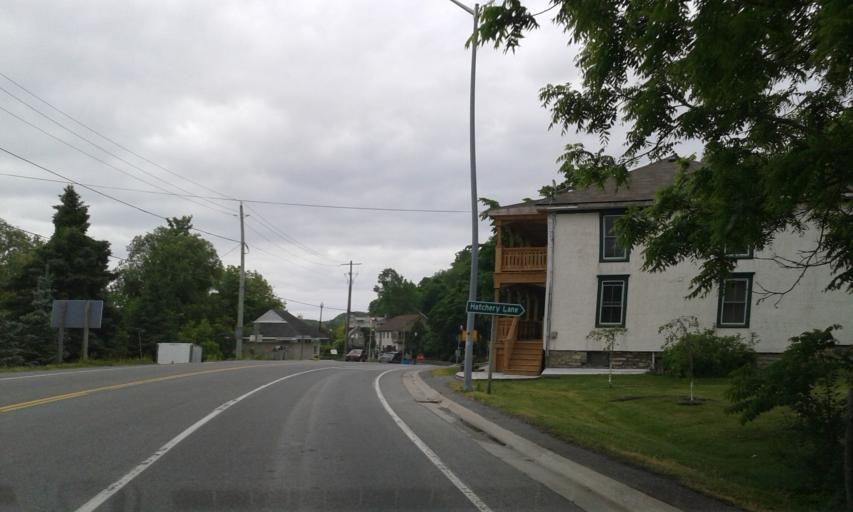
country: CA
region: Ontario
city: Picton
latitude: 44.0422
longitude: -77.0618
